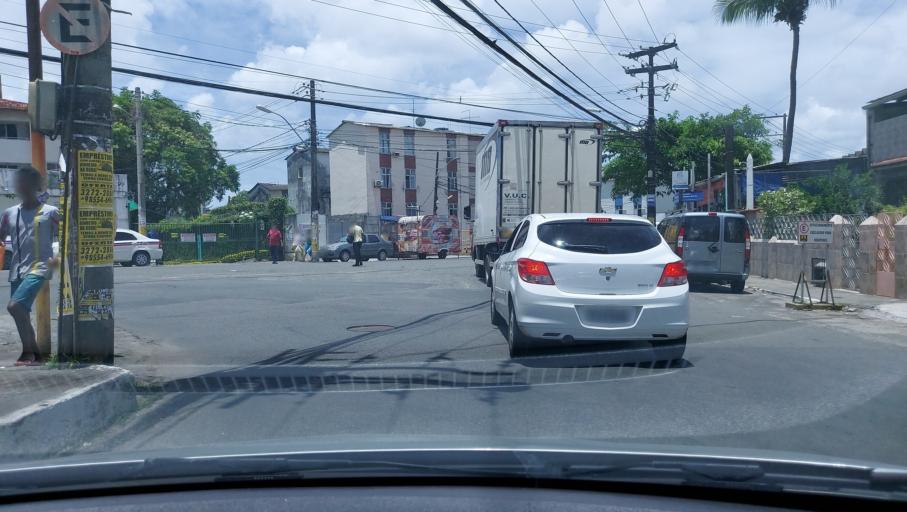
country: BR
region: Bahia
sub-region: Salvador
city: Salvador
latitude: -12.9851
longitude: -38.4778
